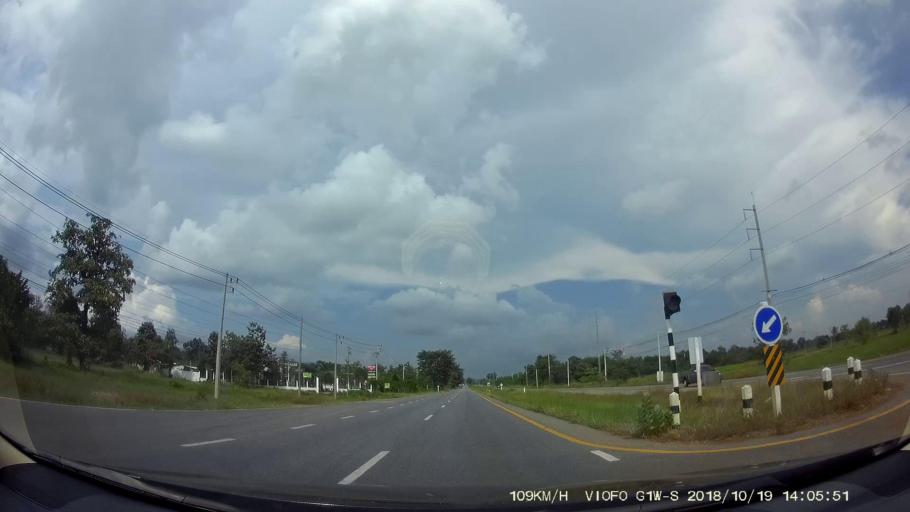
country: TH
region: Chaiyaphum
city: Chaiyaphum
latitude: 15.8801
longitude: 102.0979
